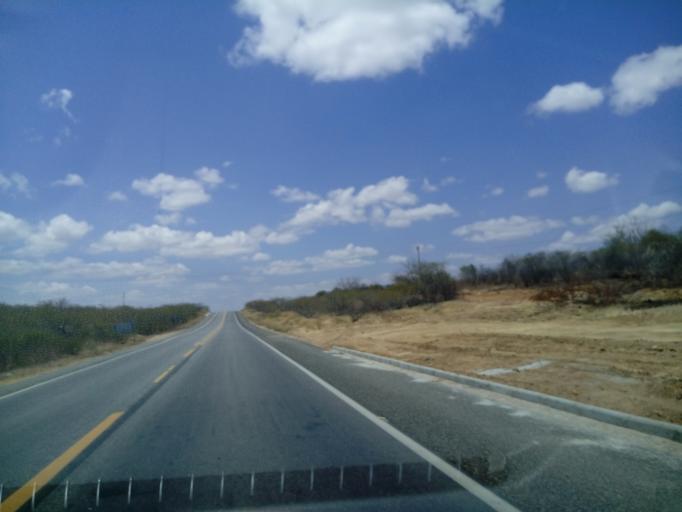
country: BR
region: Paraiba
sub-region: Patos
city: Patos
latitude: -7.0206
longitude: -37.2370
